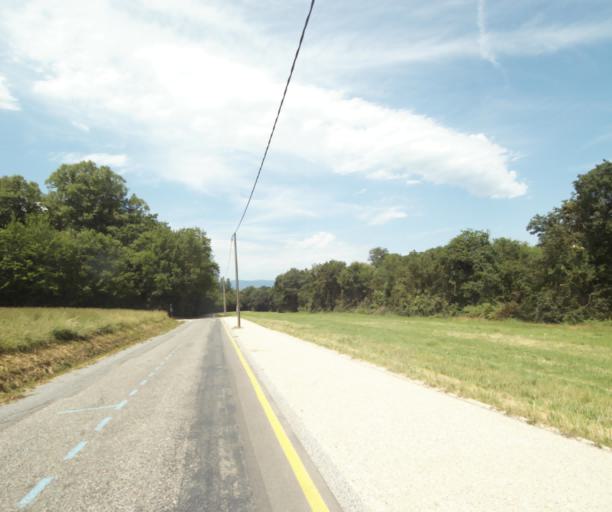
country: FR
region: Rhone-Alpes
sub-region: Departement de la Haute-Savoie
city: Chens-sur-Leman
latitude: 46.3196
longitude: 6.2647
